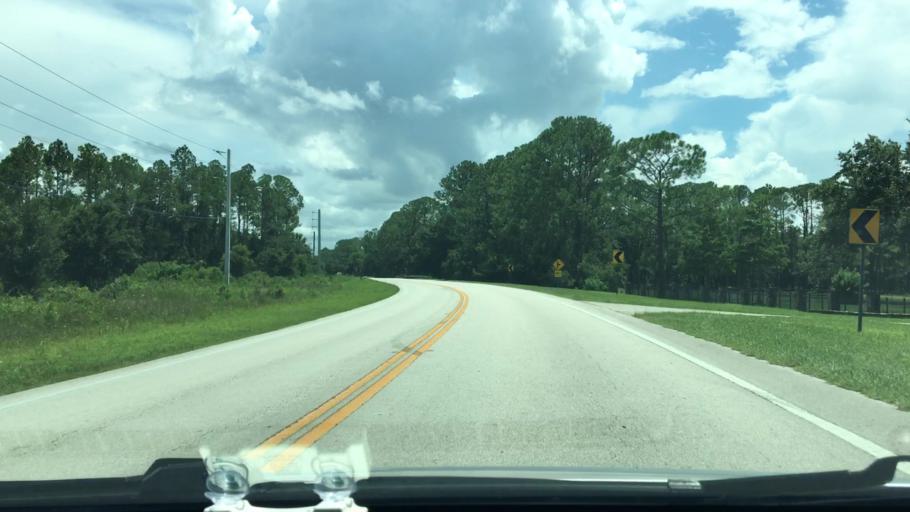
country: US
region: Florida
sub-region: Volusia County
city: Samsula-Spruce Creek
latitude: 29.0586
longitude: -81.0685
